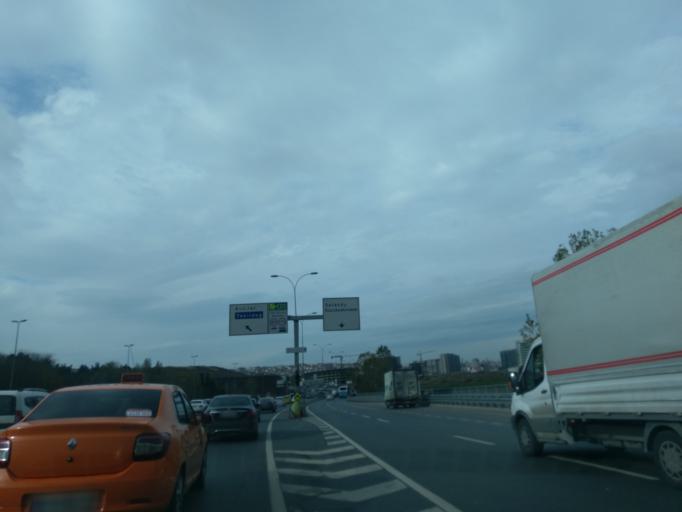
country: TR
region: Istanbul
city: Bahcelievler
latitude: 40.9951
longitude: 28.8151
